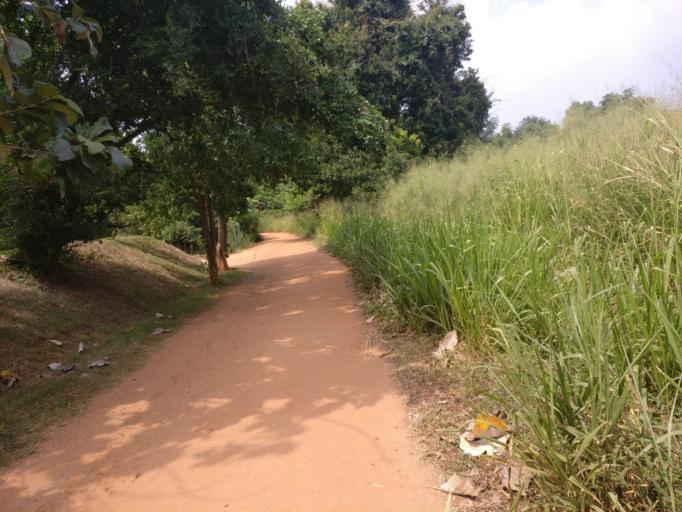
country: LK
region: Central
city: Dambulla
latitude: 7.8403
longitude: 80.6494
